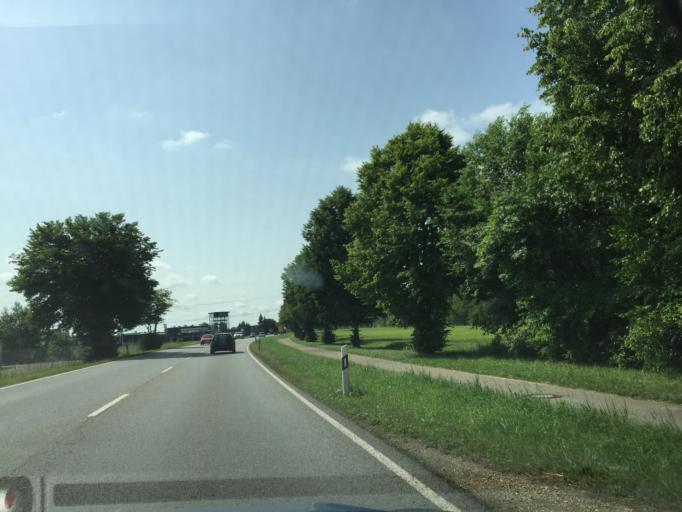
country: DE
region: Bavaria
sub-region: Swabia
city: Senden
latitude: 48.3172
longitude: 10.0526
